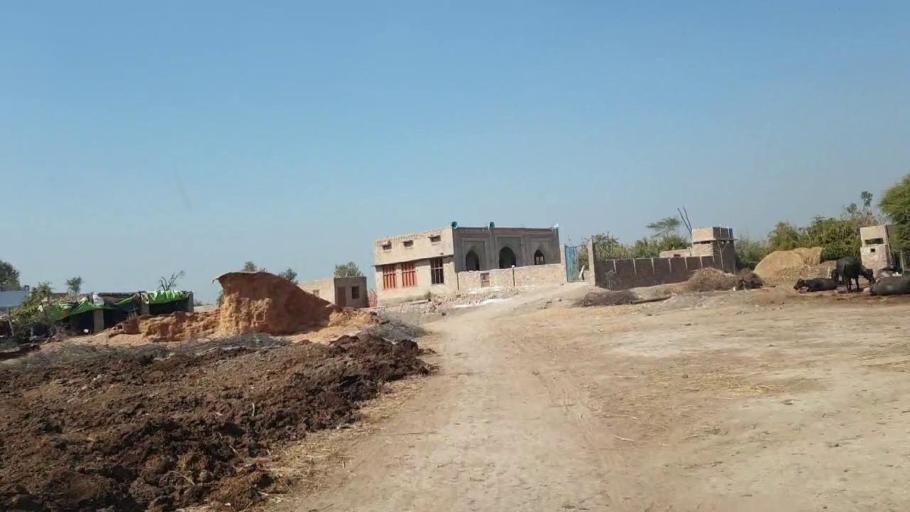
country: PK
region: Sindh
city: Bhit Shah
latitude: 25.9247
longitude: 68.4835
